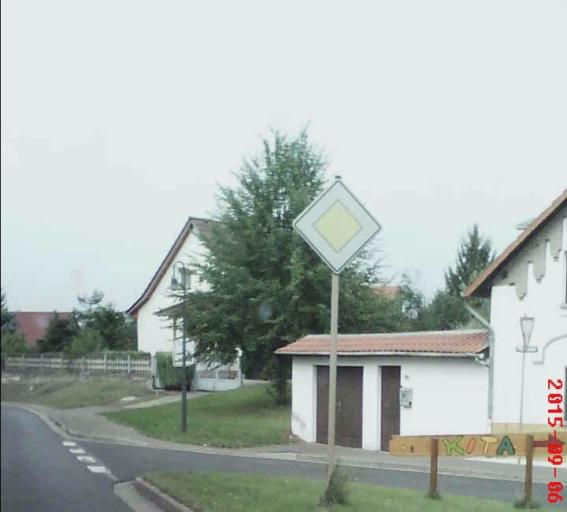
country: DE
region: Thuringia
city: Seebach
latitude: 51.1807
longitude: 10.5059
